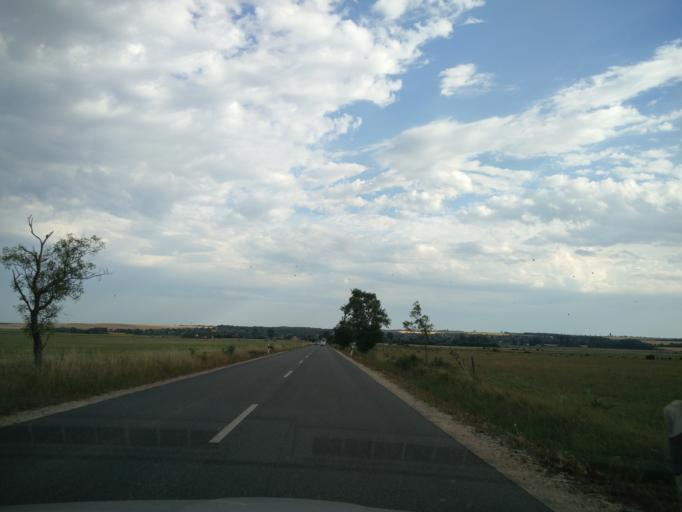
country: HU
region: Fejer
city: Zamoly
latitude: 47.3349
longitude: 18.4062
